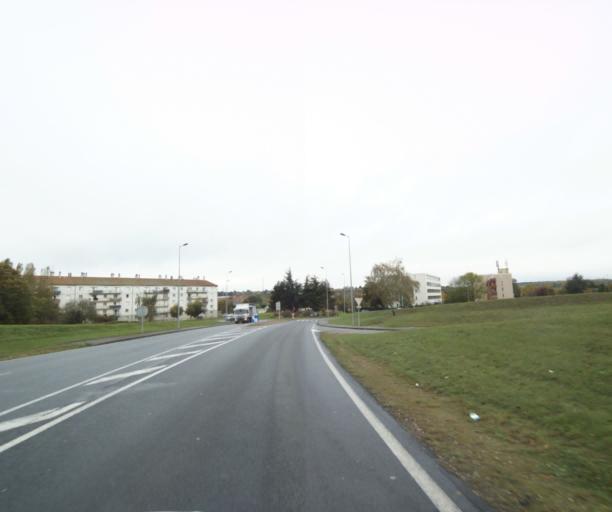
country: FR
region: Centre
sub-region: Departement d'Eure-et-Loir
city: Dreux
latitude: 48.7348
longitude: 1.3855
